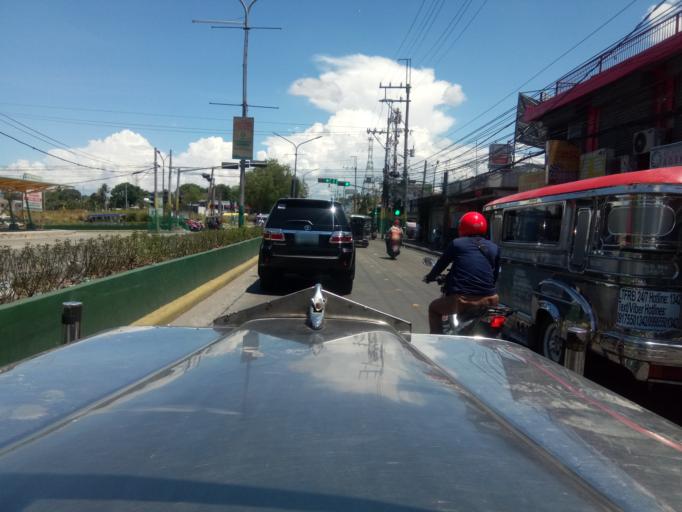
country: PH
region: Calabarzon
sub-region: Province of Cavite
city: Dasmarinas
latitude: 14.3182
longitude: 120.9643
